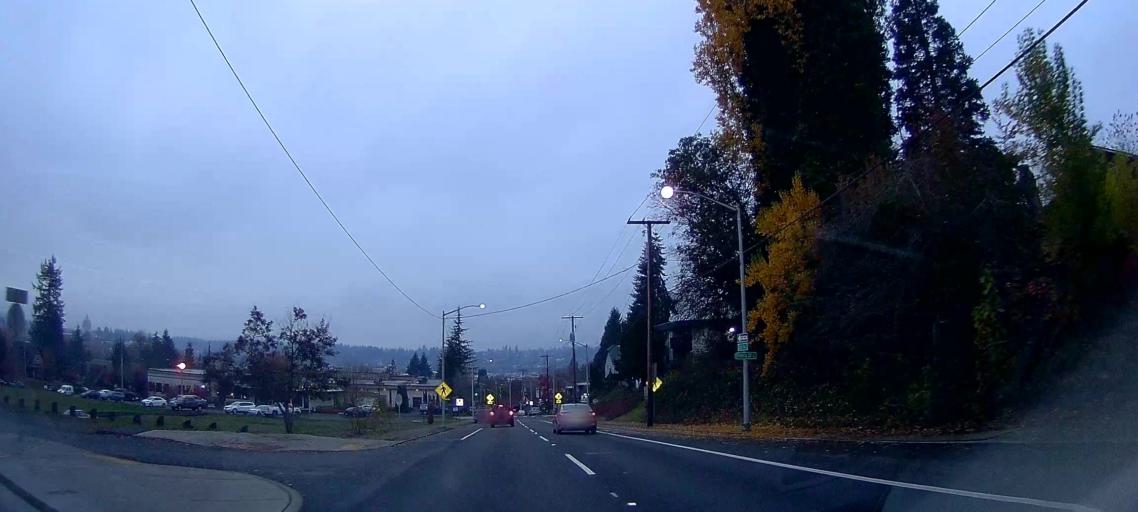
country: US
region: Washington
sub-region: Thurston County
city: Olympia
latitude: 47.0469
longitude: -122.8833
